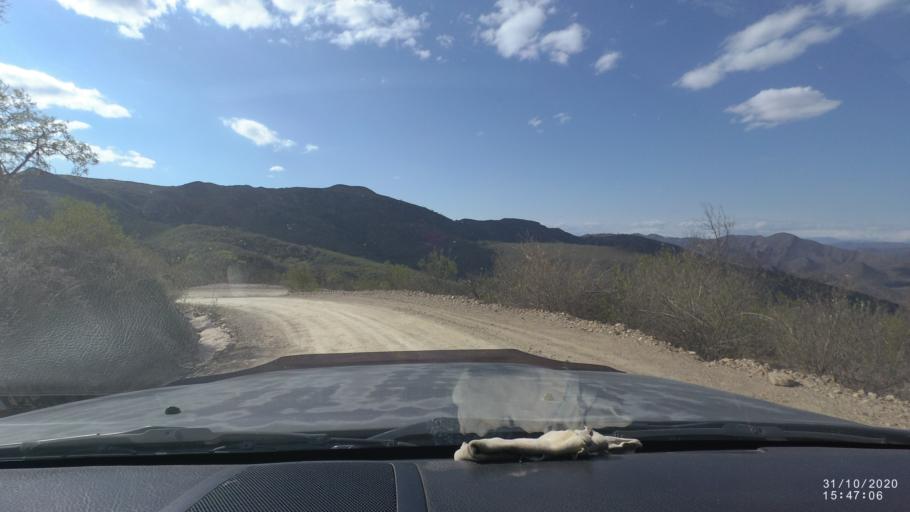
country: BO
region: Chuquisaca
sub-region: Provincia Zudanez
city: Mojocoya
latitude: -18.3144
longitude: -64.7157
